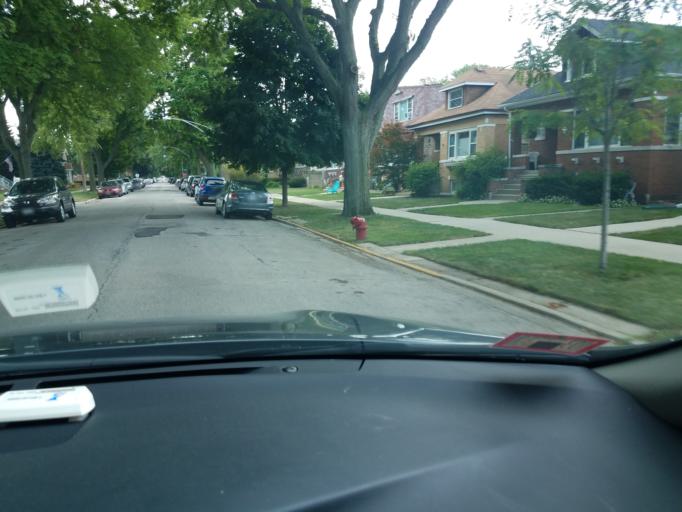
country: US
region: Illinois
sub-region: Cook County
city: Harwood Heights
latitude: 41.9859
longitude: -87.7719
